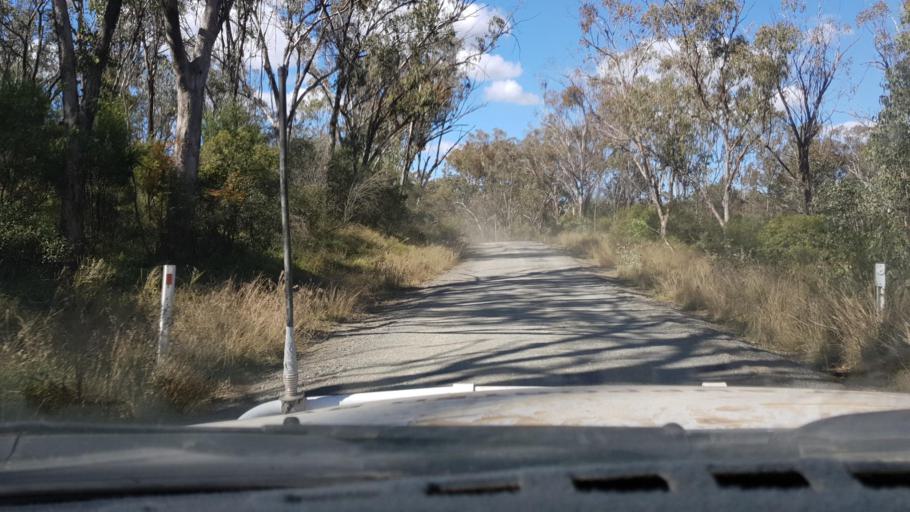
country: AU
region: New South Wales
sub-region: Tamworth Municipality
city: Manilla
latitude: -30.4797
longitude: 150.7639
